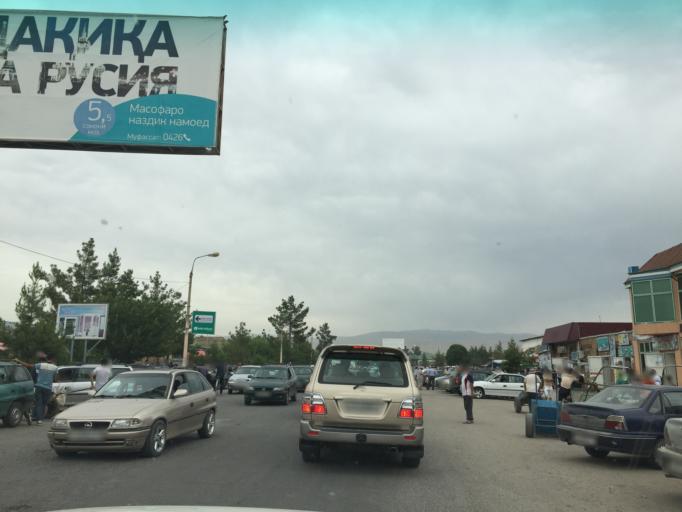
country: TJ
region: Khatlon
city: Vose'
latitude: 37.8054
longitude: 69.6400
